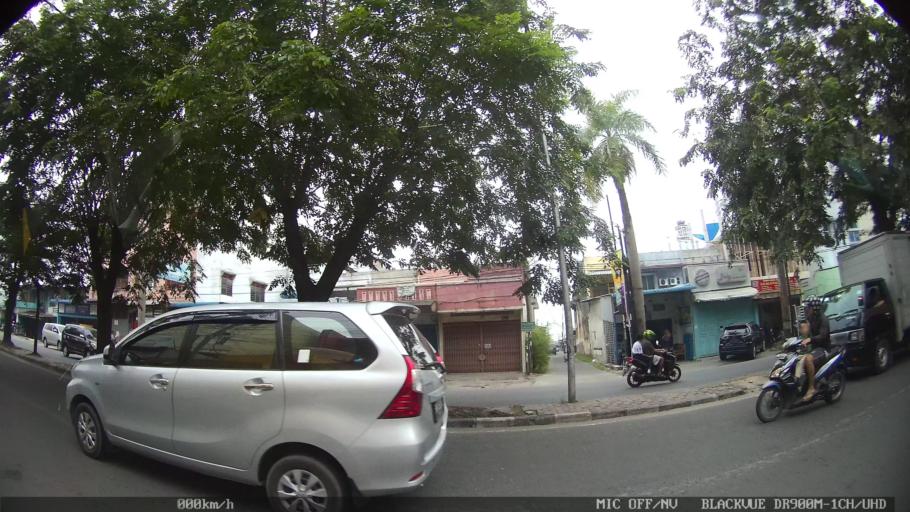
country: ID
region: North Sumatra
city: Deli Tua
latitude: 3.5469
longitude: 98.6875
